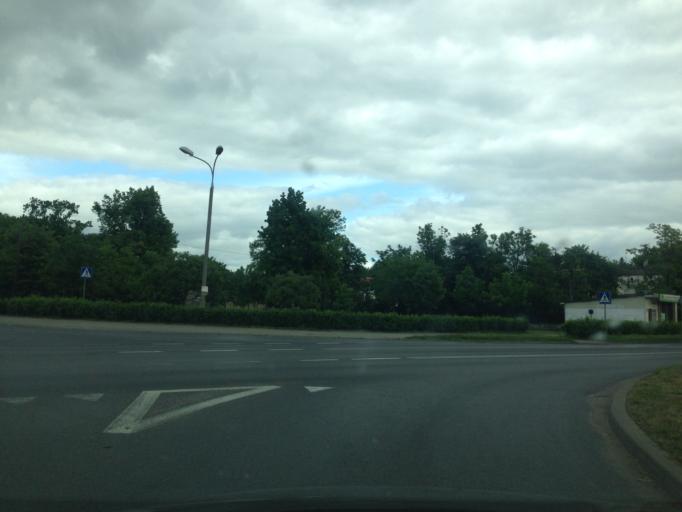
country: PL
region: Kujawsko-Pomorskie
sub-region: Powiat swiecki
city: Swiecie
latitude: 53.4010
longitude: 18.4038
